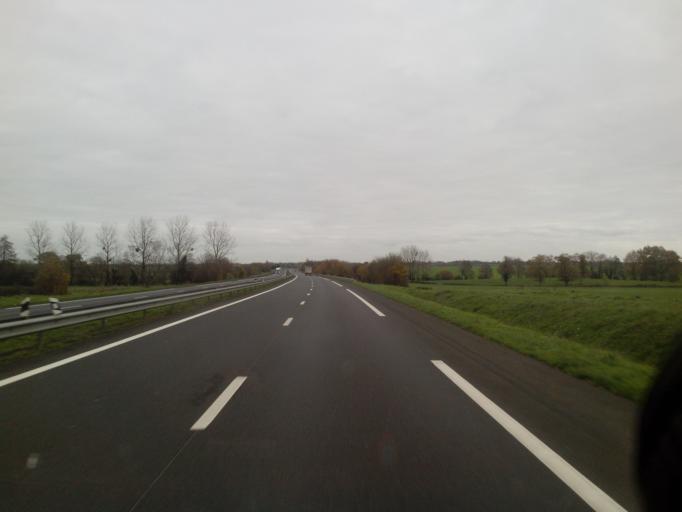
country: FR
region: Pays de la Loire
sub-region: Departement de Maine-et-Loire
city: Roussay
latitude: 47.1112
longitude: -1.0482
